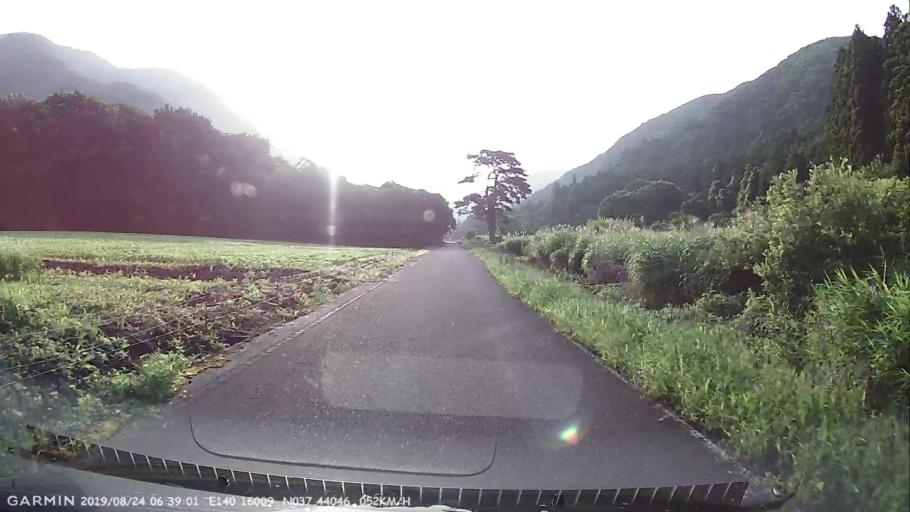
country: JP
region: Fukushima
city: Inawashiro
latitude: 37.4404
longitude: 140.1602
